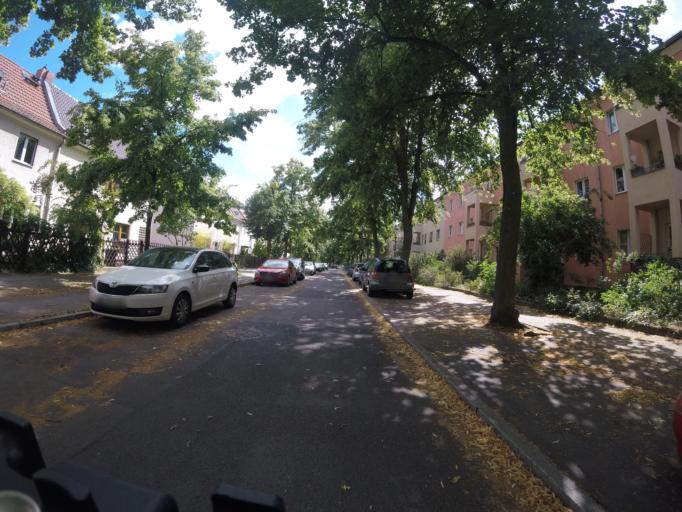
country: DE
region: Berlin
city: Wilhelmstadt
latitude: 52.5151
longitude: 13.1986
